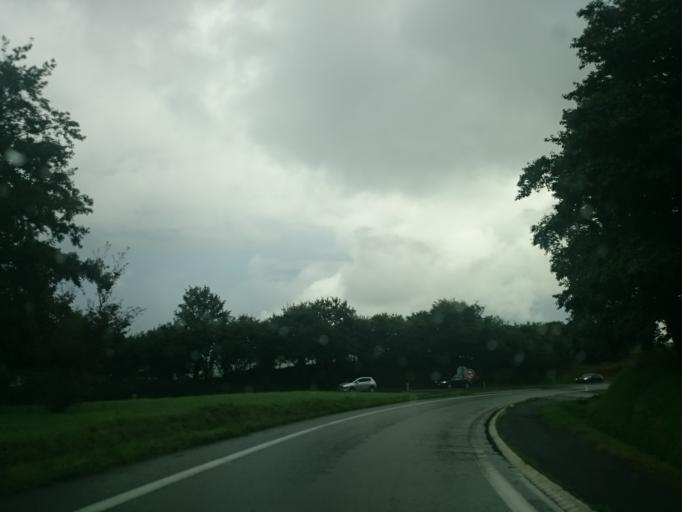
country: FR
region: Brittany
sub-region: Departement du Finistere
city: Gouesnou
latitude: 48.4347
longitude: -4.4445
